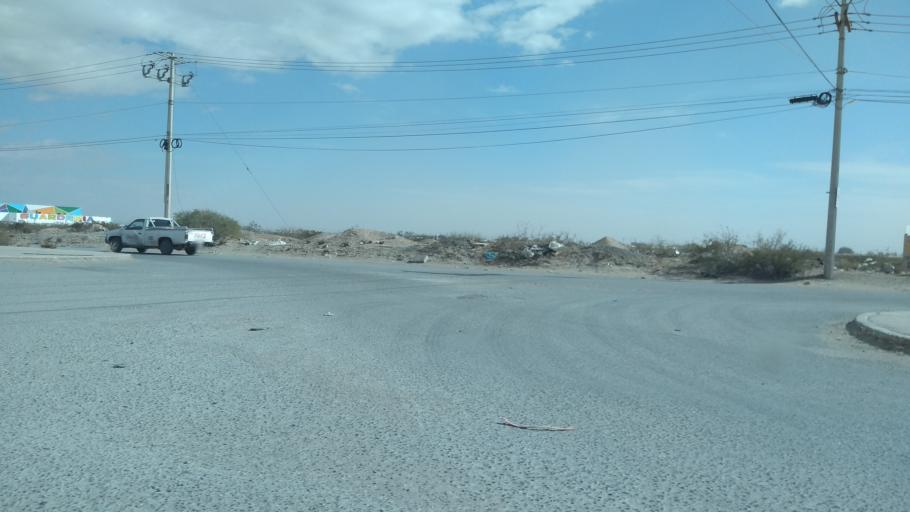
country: US
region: Texas
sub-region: El Paso County
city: San Elizario
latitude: 31.5714
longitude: -106.3407
